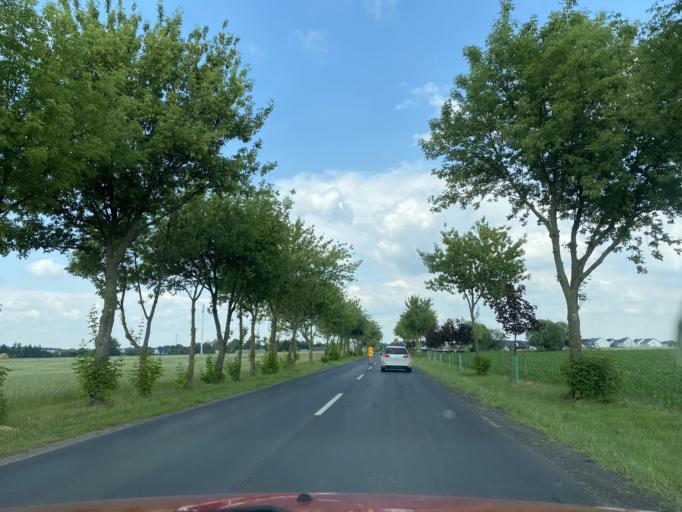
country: PL
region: Greater Poland Voivodeship
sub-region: Powiat poznanski
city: Dopiewo
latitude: 52.3644
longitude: 16.7297
